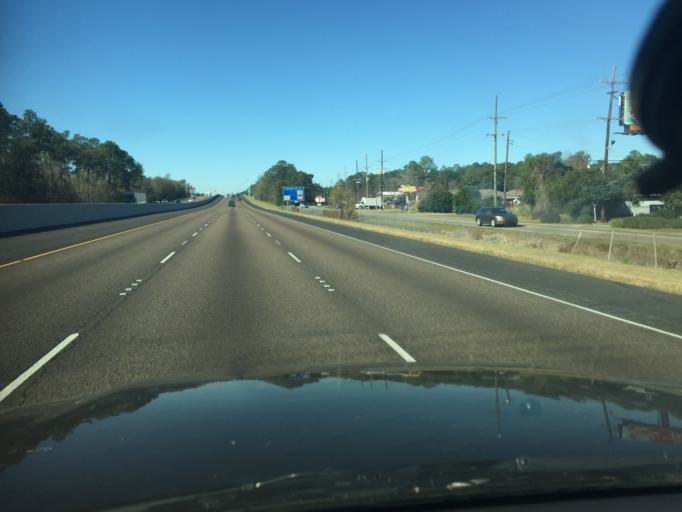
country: US
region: Louisiana
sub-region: Saint Tammany Parish
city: Slidell
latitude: 30.3102
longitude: -89.7632
